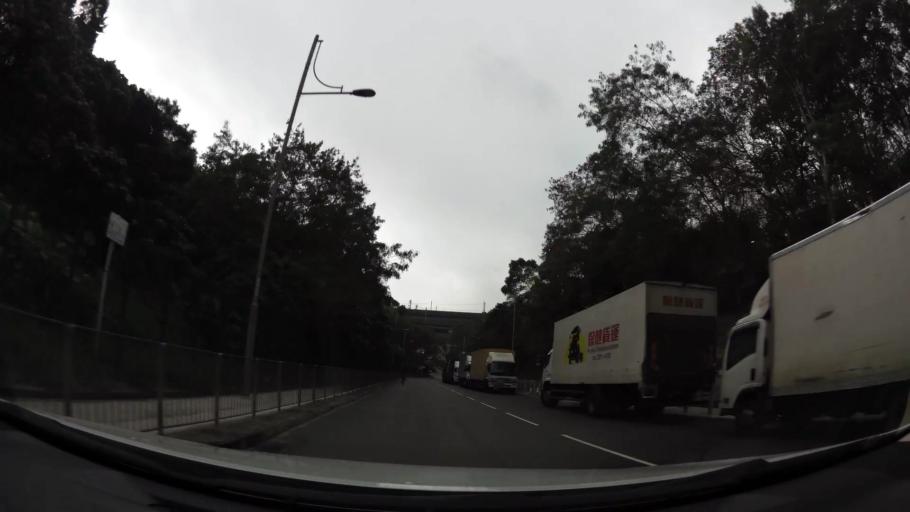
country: HK
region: Tsuen Wan
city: Tsuen Wan
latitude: 22.3565
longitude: 114.1183
